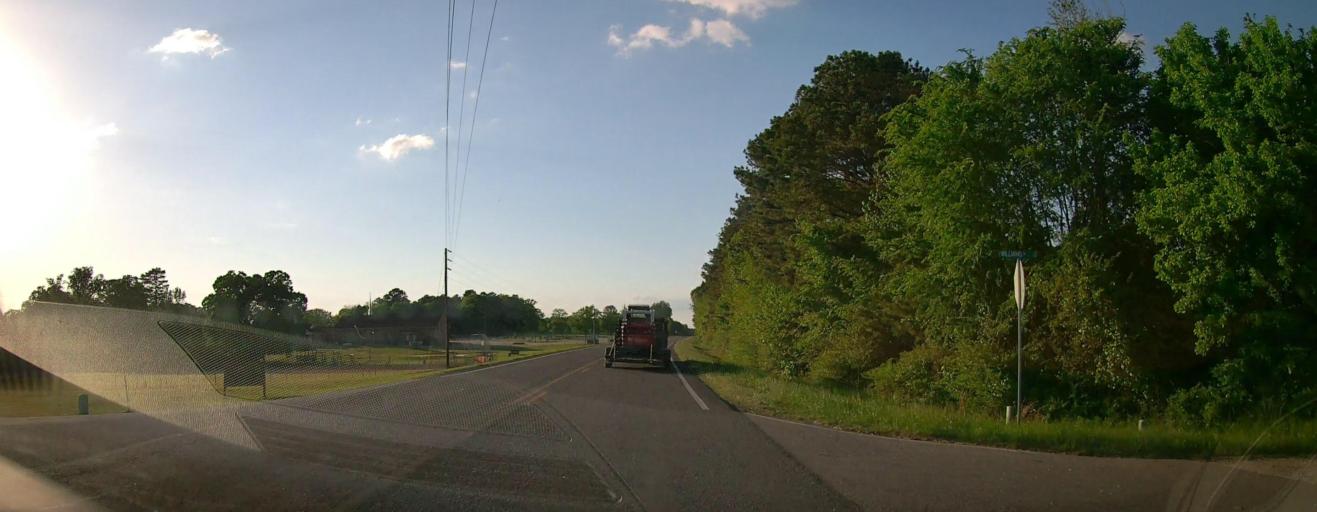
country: US
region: Georgia
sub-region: Jasper County
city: Monticello
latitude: 33.4717
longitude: -83.6406
